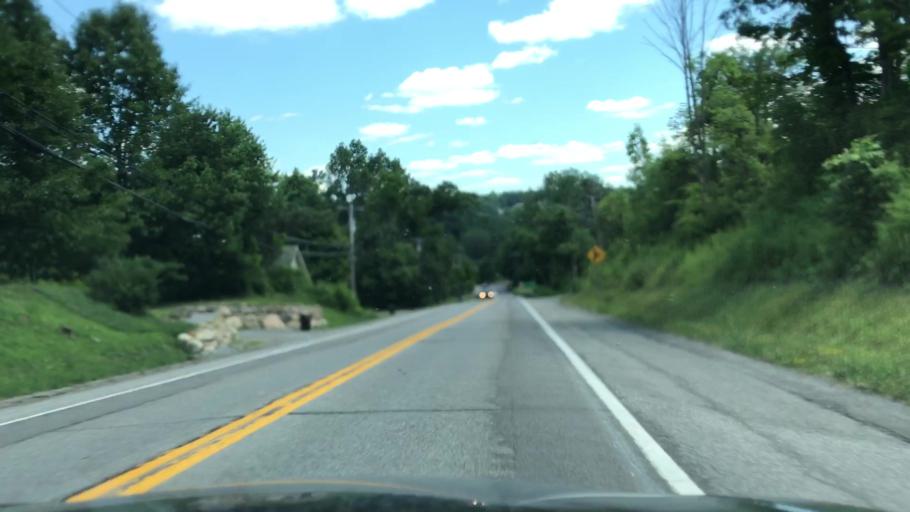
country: US
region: New York
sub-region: Erie County
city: East Aurora
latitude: 42.7684
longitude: -78.5369
